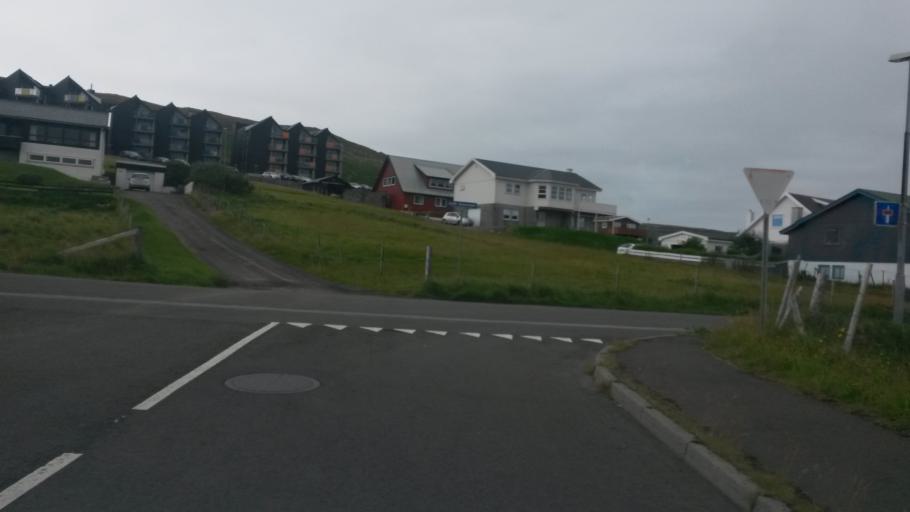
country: FO
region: Streymoy
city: Argir
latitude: 62.0010
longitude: -6.8046
